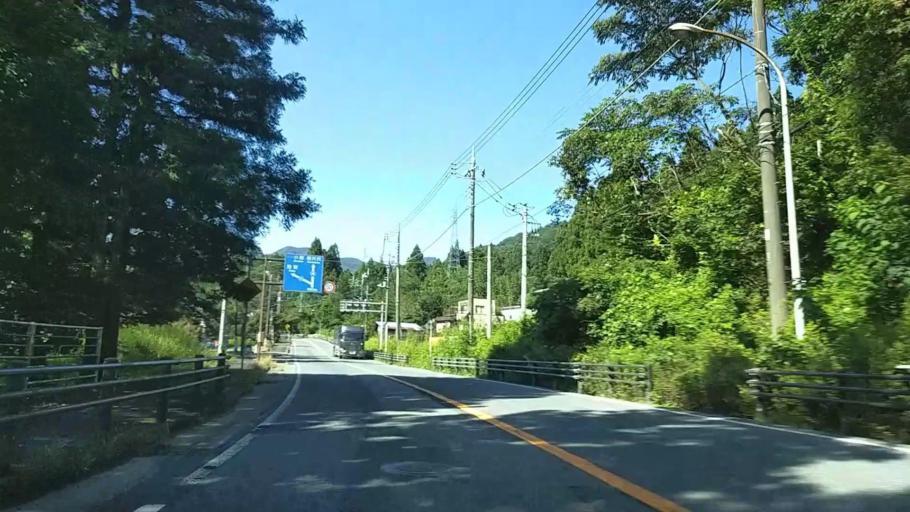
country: JP
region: Gunma
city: Annaka
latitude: 36.3285
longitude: 138.7087
